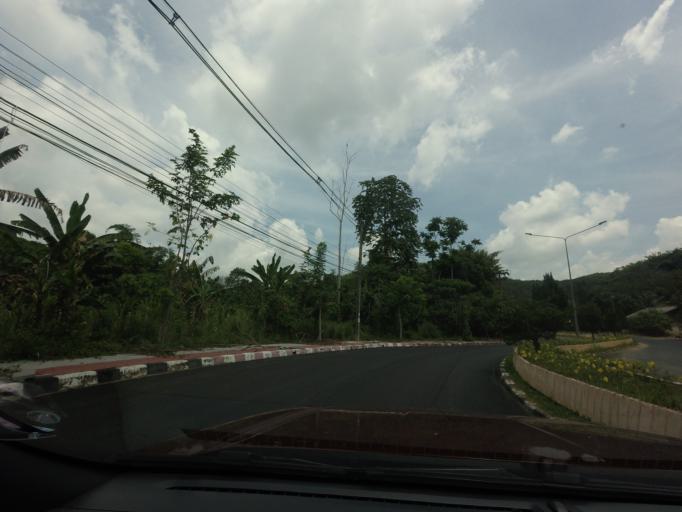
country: TH
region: Yala
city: Betong
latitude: 5.7522
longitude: 101.0428
